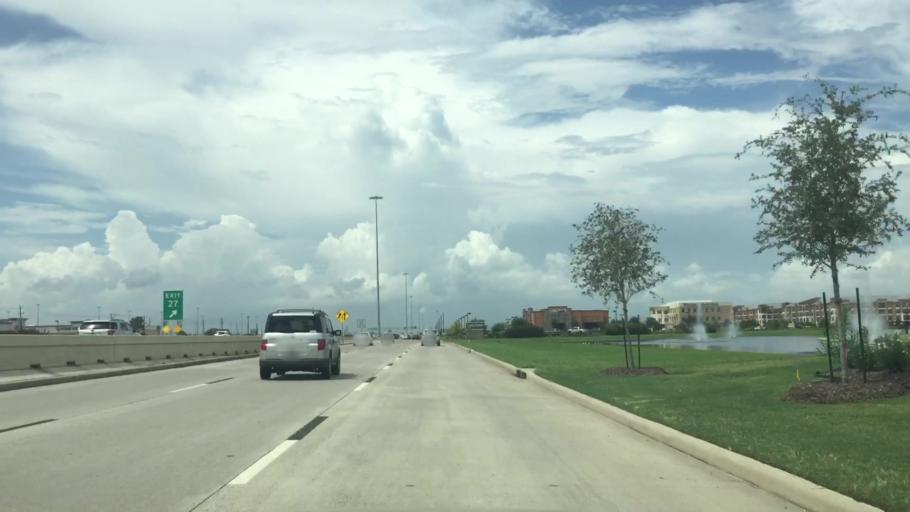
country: US
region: Texas
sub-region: Harris County
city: Webster
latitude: 29.5435
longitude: -95.1437
